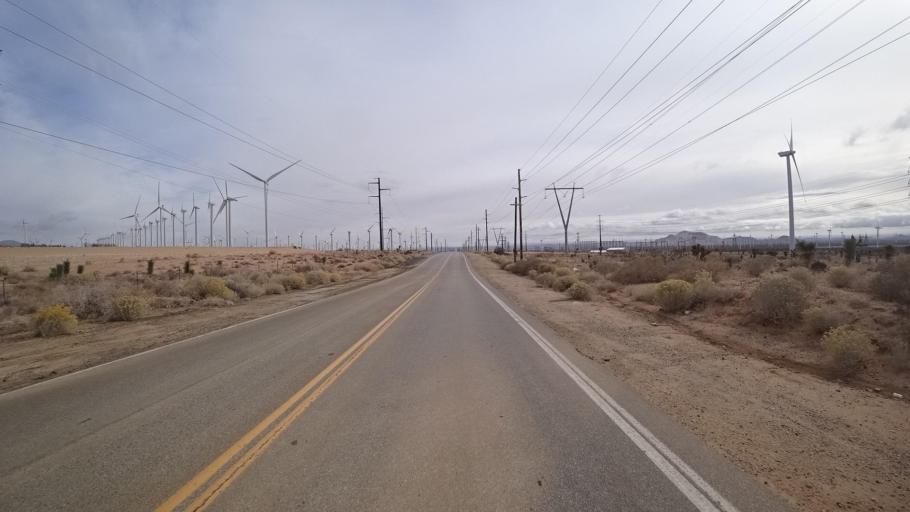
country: US
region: California
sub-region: Kern County
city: Mojave
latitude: 35.0383
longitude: -118.2923
